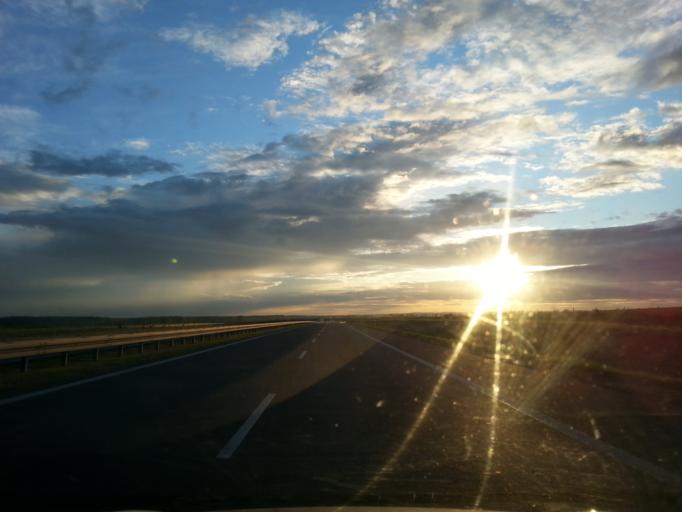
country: PL
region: Lower Silesian Voivodeship
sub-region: Powiat olesnicki
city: Sycow
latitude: 51.2977
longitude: 17.6616
